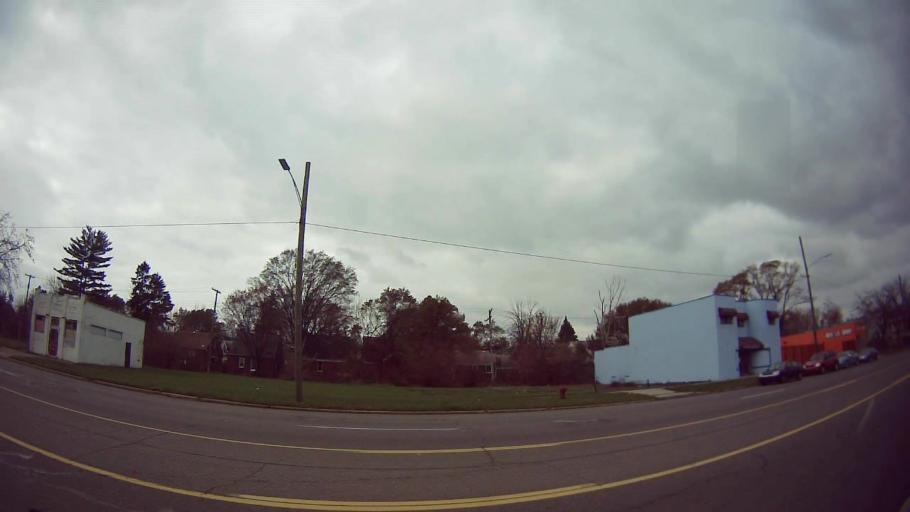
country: US
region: Michigan
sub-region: Macomb County
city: Warren
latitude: 42.4373
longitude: -83.0243
